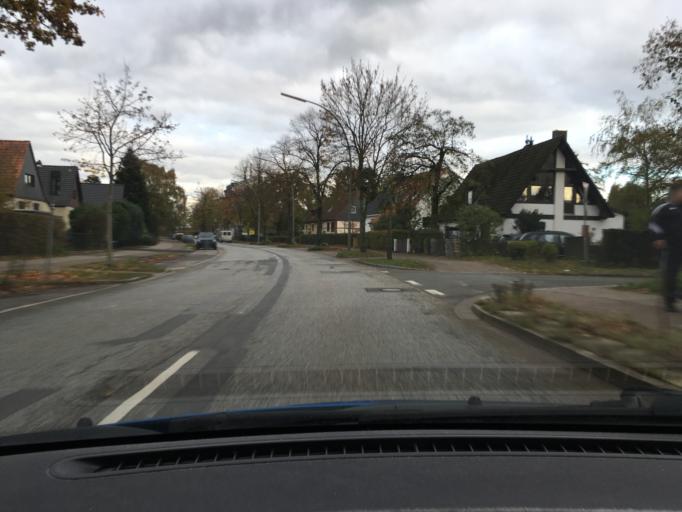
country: DE
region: Hamburg
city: Harburg
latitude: 53.4920
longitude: 10.0149
